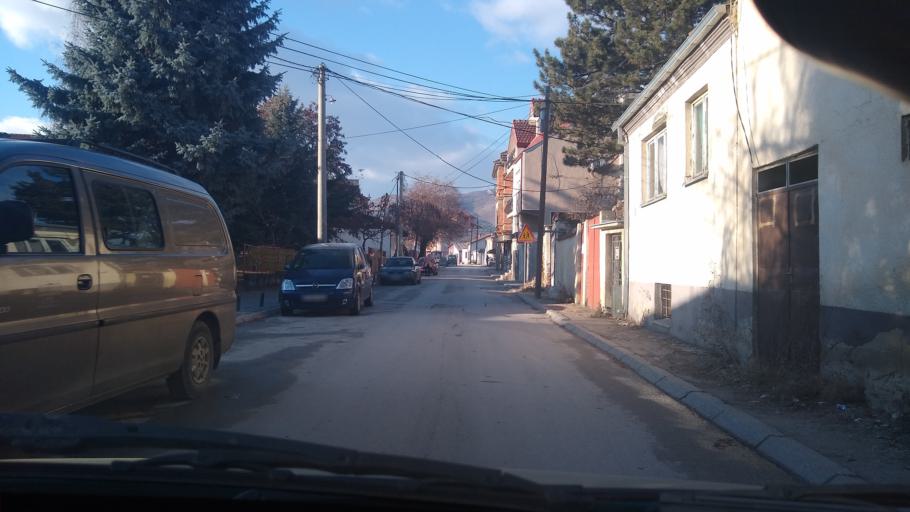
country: MK
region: Bitola
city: Bitola
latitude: 41.0272
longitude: 21.3275
